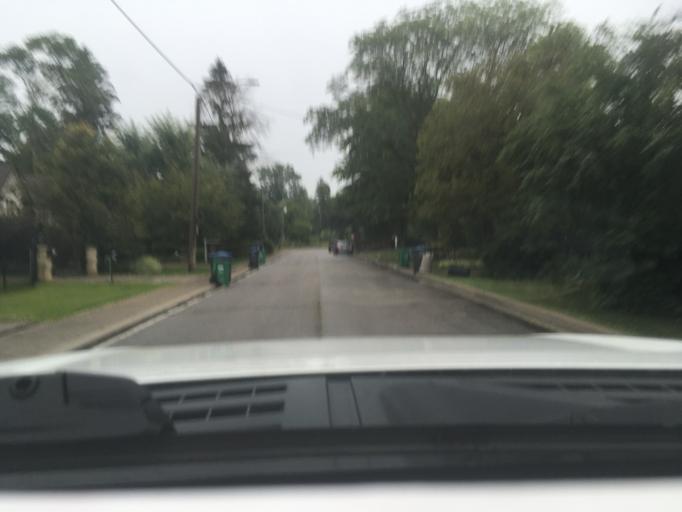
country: CA
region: Ontario
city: Mississauga
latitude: 43.5457
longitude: -79.6150
